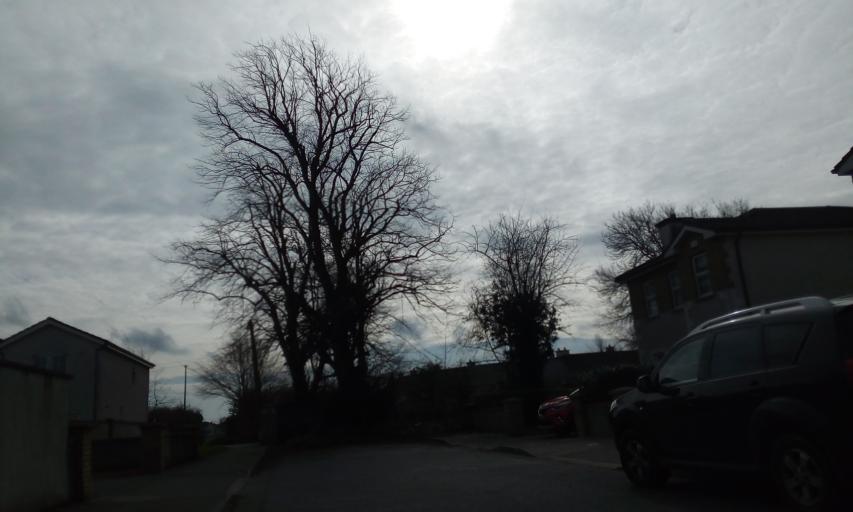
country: IE
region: Leinster
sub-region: Kilkenny
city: Kilkenny
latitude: 52.6659
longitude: -7.2349
